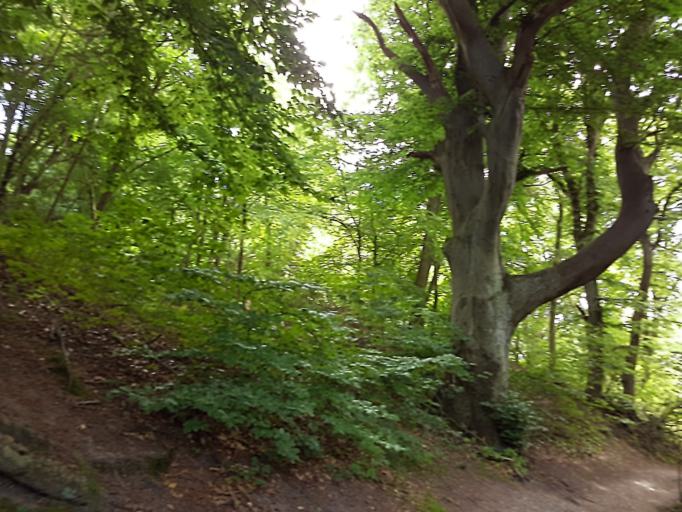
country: DK
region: Capital Region
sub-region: Fureso Kommune
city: Farum
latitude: 55.8035
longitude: 12.3399
